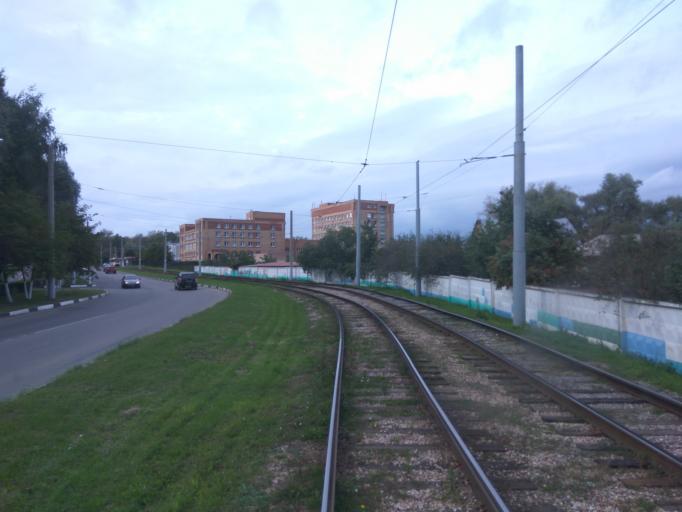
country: RU
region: Moskovskaya
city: Kolomna
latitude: 55.0651
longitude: 38.7564
